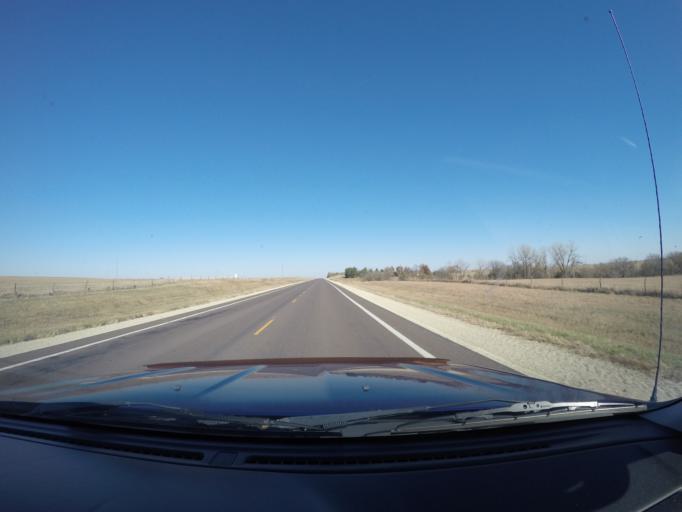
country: US
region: Kansas
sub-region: Marshall County
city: Blue Rapids
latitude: 39.6516
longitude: -96.7505
